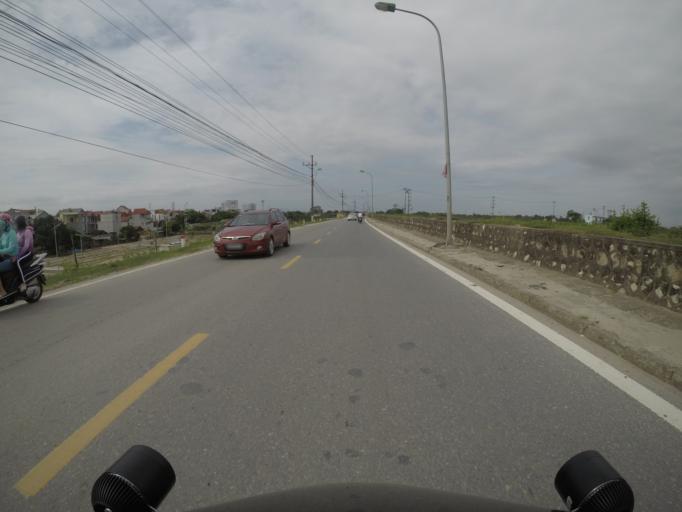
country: VN
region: Ha Noi
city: Cau Dien
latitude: 21.0869
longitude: 105.7537
